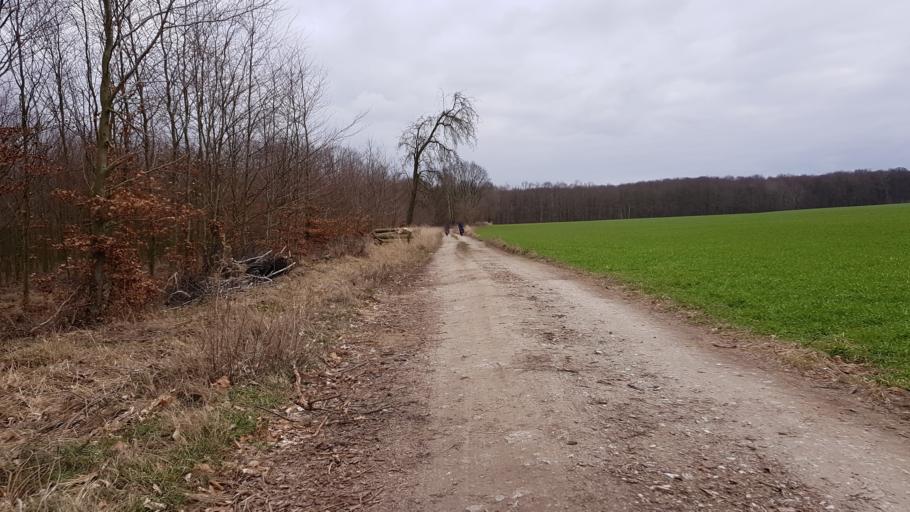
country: PL
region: West Pomeranian Voivodeship
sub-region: Powiat gryfinski
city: Banie
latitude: 53.0749
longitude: 14.7292
